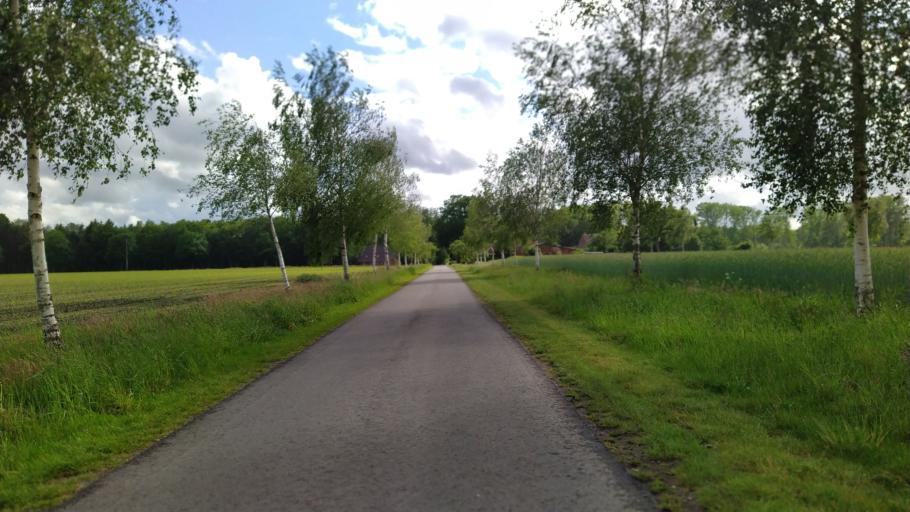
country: DE
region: Lower Saxony
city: Brest
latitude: 53.4362
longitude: 9.3559
